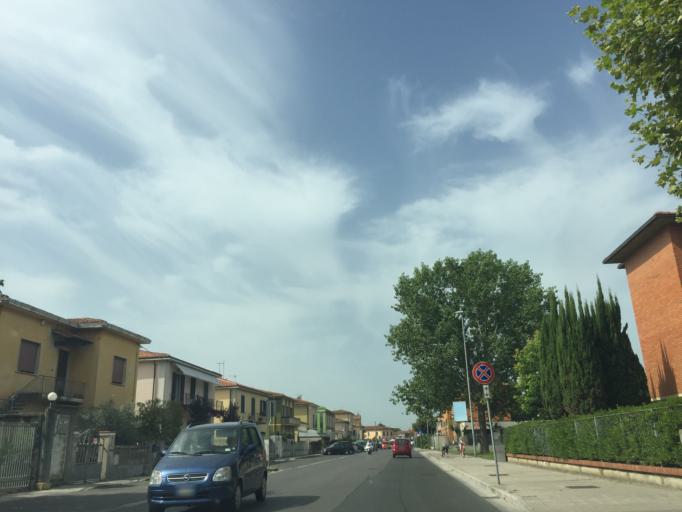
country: IT
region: Tuscany
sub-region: Province of Pisa
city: Pisa
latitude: 43.7192
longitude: 10.3845
